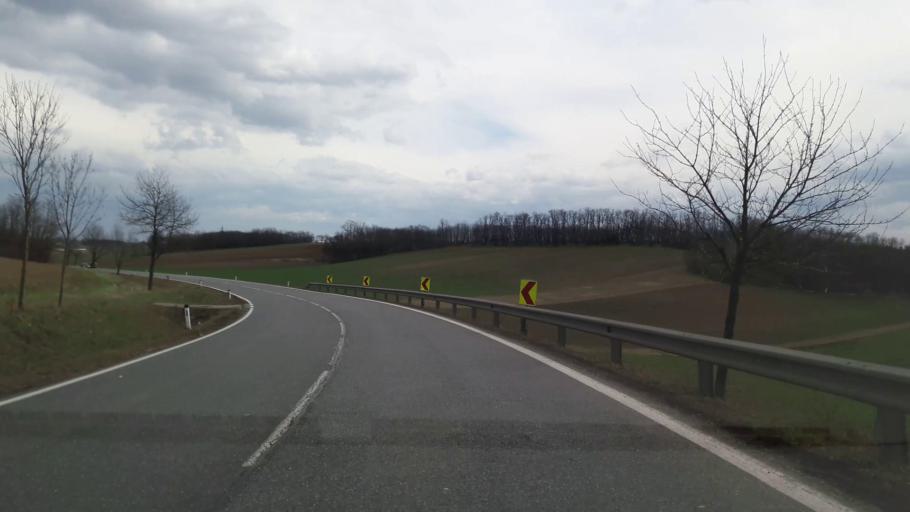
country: AT
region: Lower Austria
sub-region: Politischer Bezirk Mistelbach
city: Mistelbach
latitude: 48.5261
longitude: 16.6033
